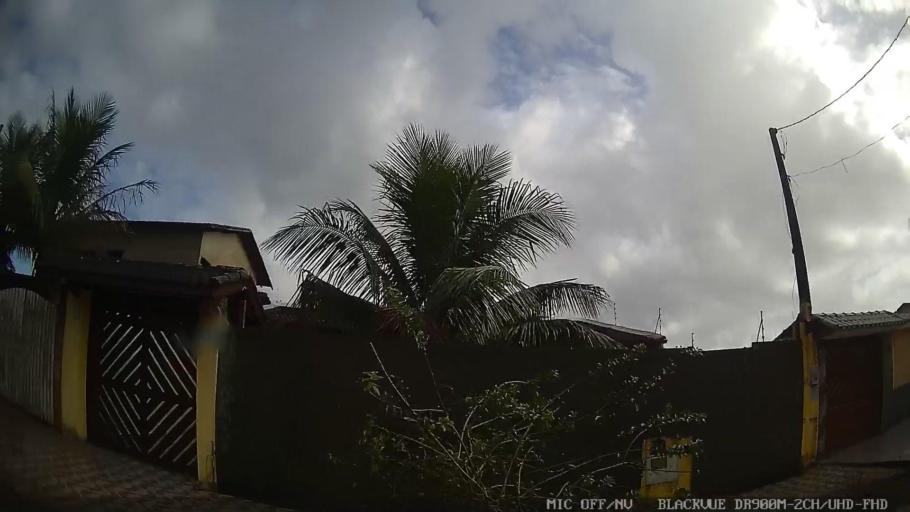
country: BR
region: Sao Paulo
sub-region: Itanhaem
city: Itanhaem
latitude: -24.2026
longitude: -46.8324
